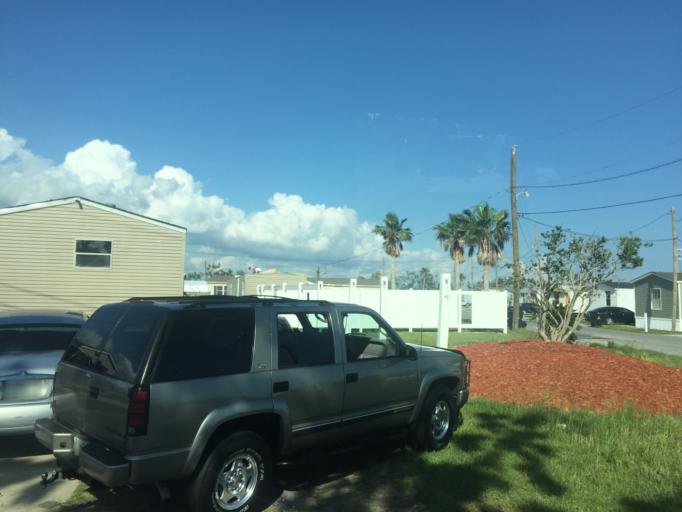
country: US
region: Florida
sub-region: Bay County
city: Springfield
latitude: 30.1585
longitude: -85.6208
